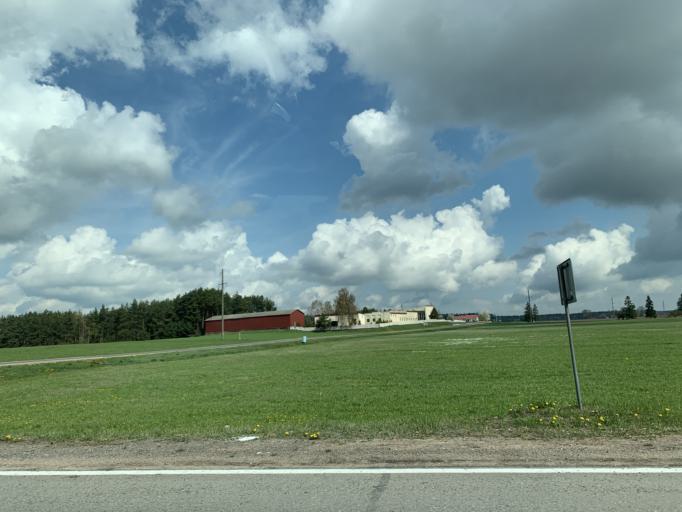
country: BY
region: Minsk
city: Nyasvizh
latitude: 53.2510
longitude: 26.6879
